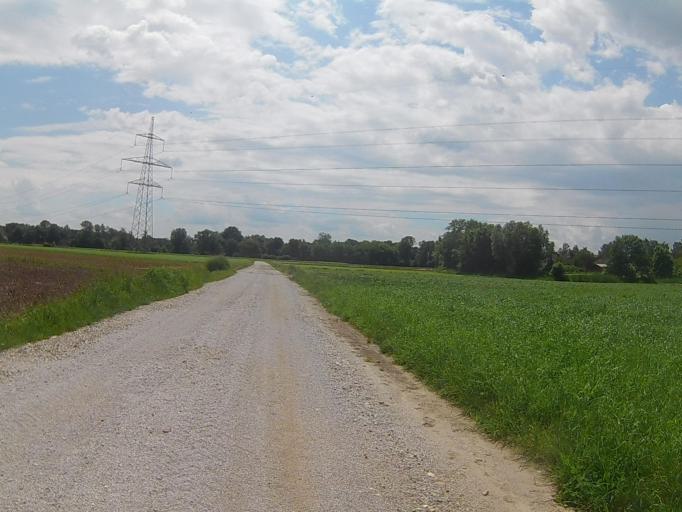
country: SI
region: Duplek
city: Zgornji Duplek
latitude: 46.5029
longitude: 15.7222
